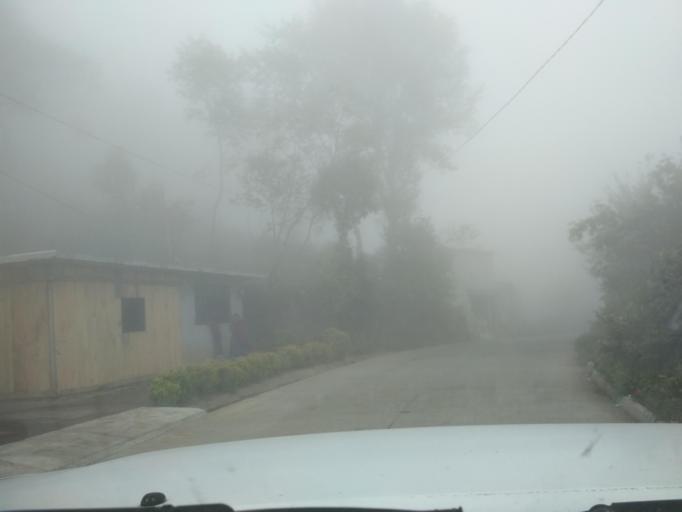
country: MX
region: Veracruz
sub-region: La Perla
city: Chilapa
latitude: 18.9784
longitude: -97.1886
